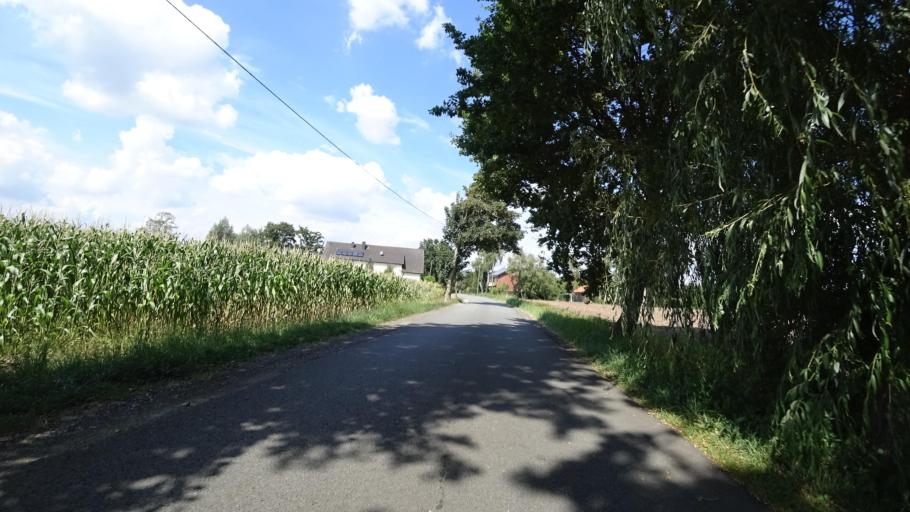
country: DE
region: North Rhine-Westphalia
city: Rietberg
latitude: 51.8733
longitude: 8.4404
